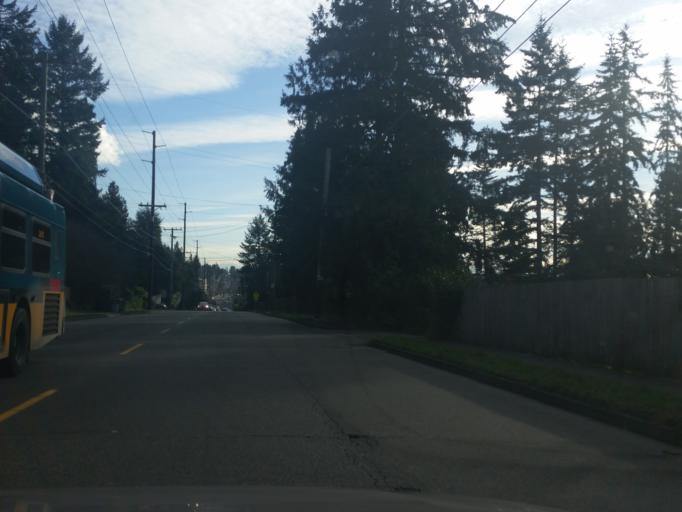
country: US
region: Washington
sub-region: King County
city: Shoreline
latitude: 47.7152
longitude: -122.3236
